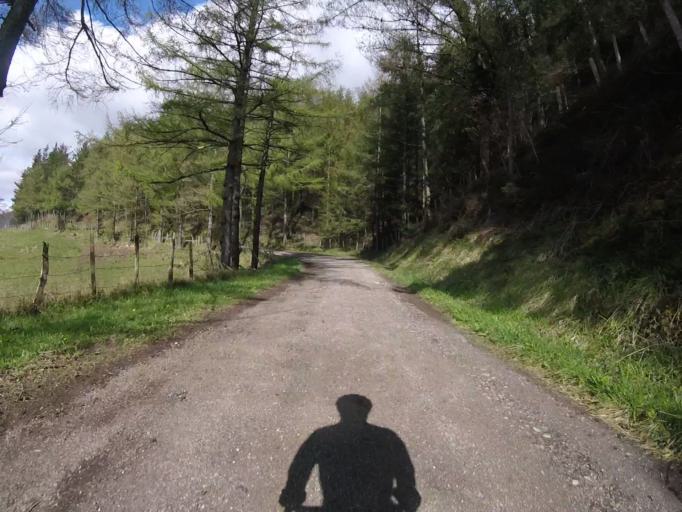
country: ES
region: Basque Country
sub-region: Provincia de Guipuzcoa
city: Albiztur
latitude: 43.1406
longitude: -2.1190
